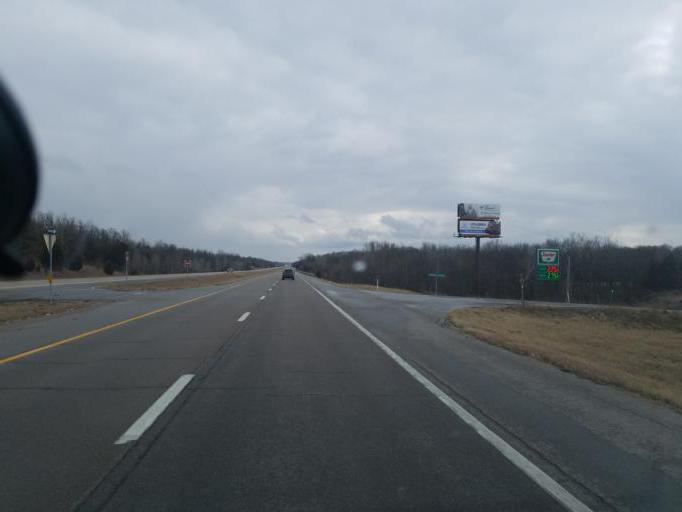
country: US
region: Missouri
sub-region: Boone County
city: Hallsville
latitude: 39.0859
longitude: -92.3299
